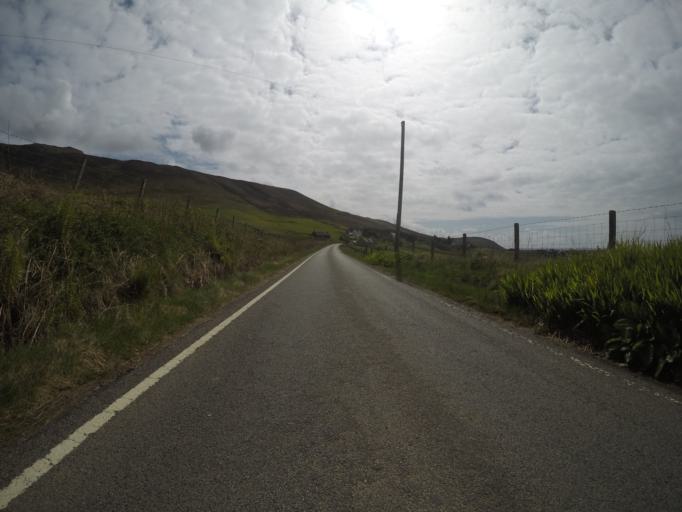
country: GB
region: Scotland
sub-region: Highland
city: Portree
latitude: 57.6147
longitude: -6.3712
